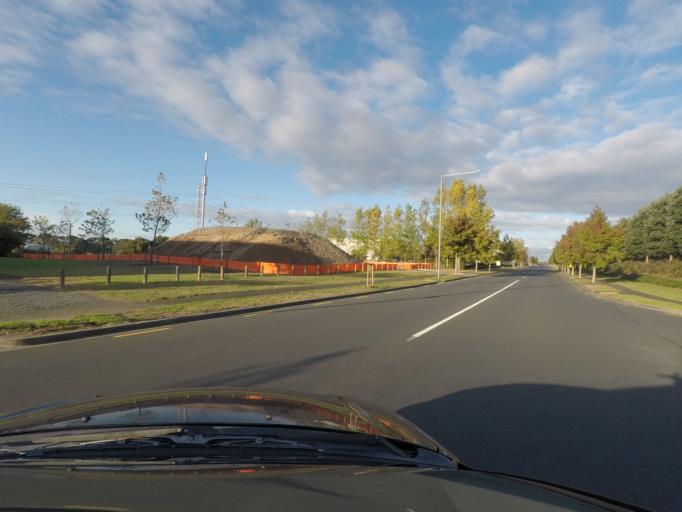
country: NZ
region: Auckland
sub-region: Auckland
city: Manukau City
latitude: -36.9421
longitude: 174.8760
